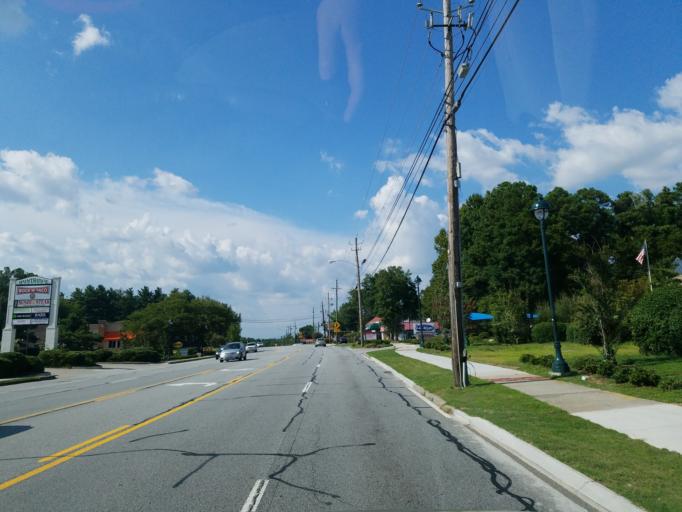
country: US
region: Georgia
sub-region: Fulton County
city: Roswell
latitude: 33.9862
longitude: -84.3507
